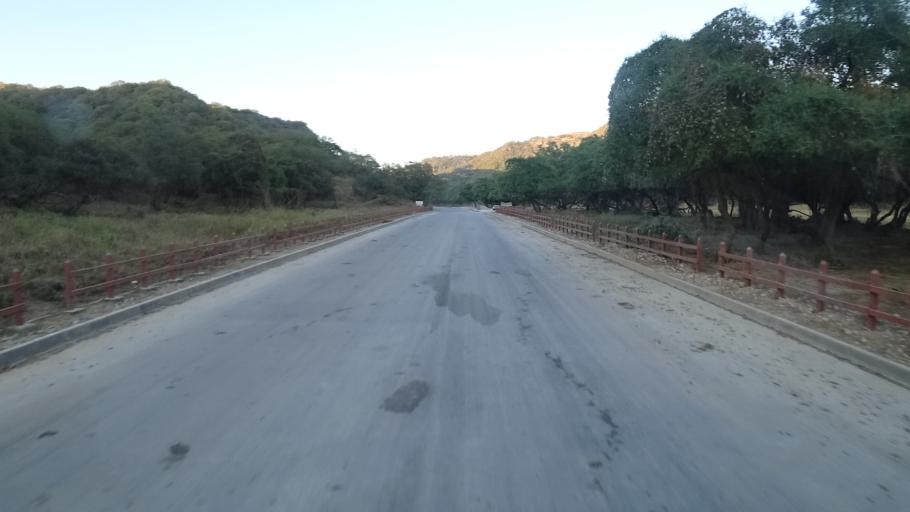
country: OM
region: Zufar
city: Salalah
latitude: 17.0960
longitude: 54.4492
